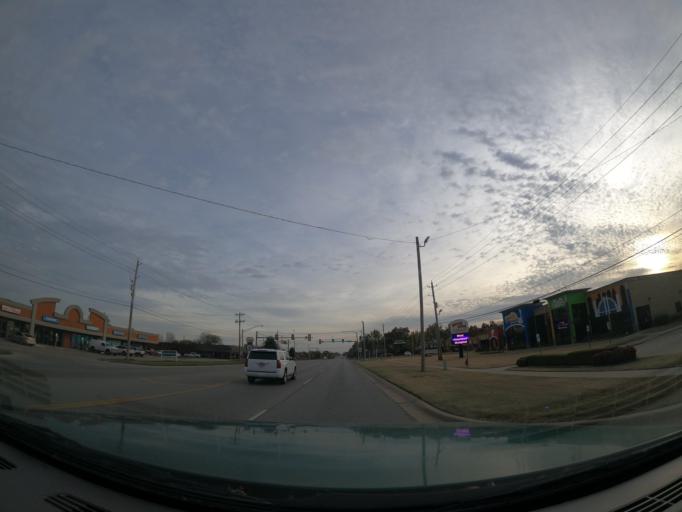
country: US
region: Oklahoma
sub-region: Tulsa County
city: Broken Arrow
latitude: 36.0550
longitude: -95.8154
